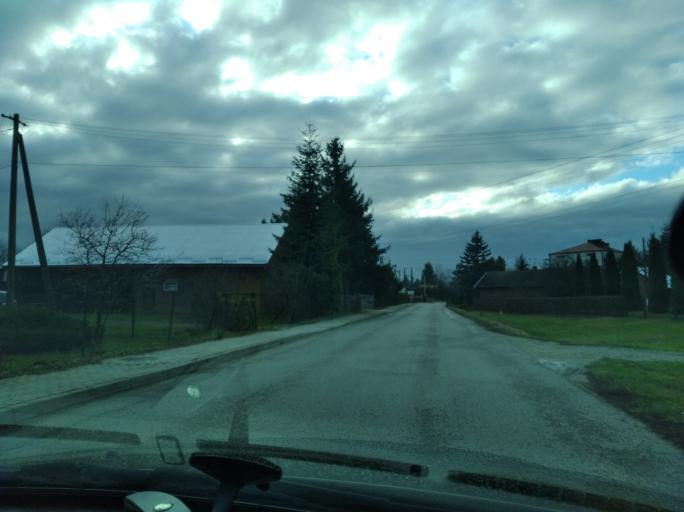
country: PL
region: Subcarpathian Voivodeship
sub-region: Powiat lancucki
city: Gluchow
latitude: 50.1071
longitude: 22.2798
